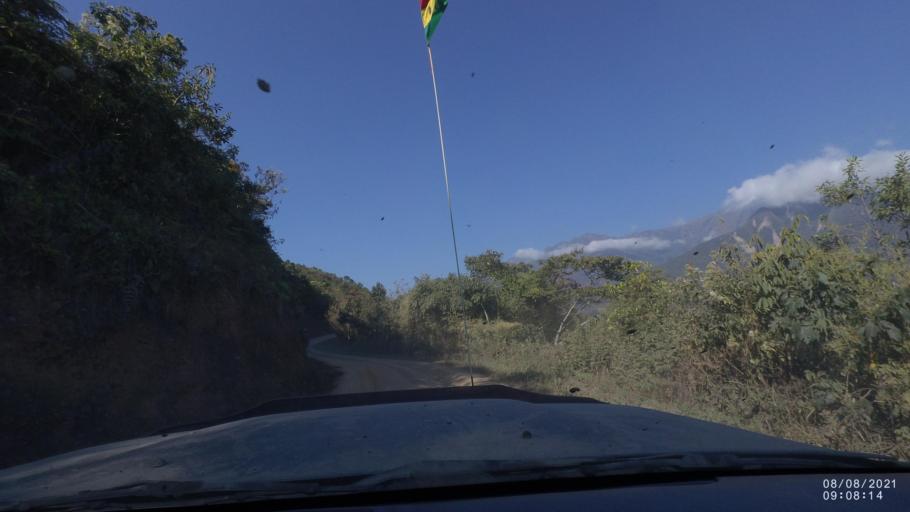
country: BO
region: La Paz
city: Quime
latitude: -16.5643
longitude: -66.7321
